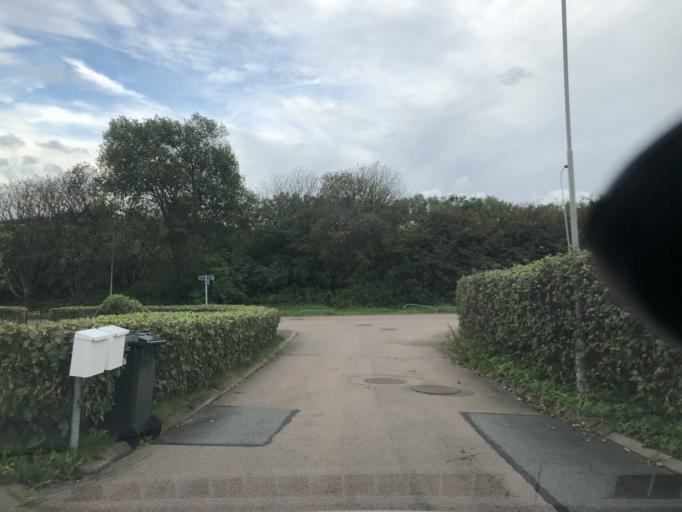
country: SE
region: Vaestra Goetaland
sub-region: Goteborg
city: Goeteborg
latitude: 57.7557
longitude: 11.9630
